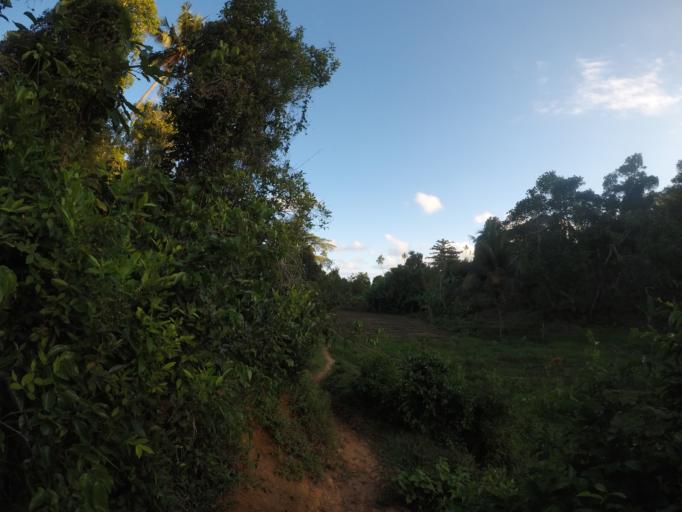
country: TZ
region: Pemba South
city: Mtambile
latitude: -5.3780
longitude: 39.7049
